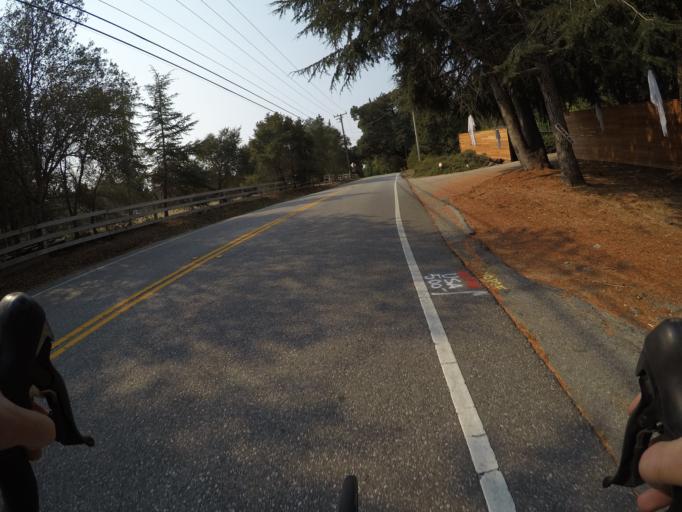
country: US
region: California
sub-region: Santa Cruz County
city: Scotts Valley
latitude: 37.0277
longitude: -122.0192
